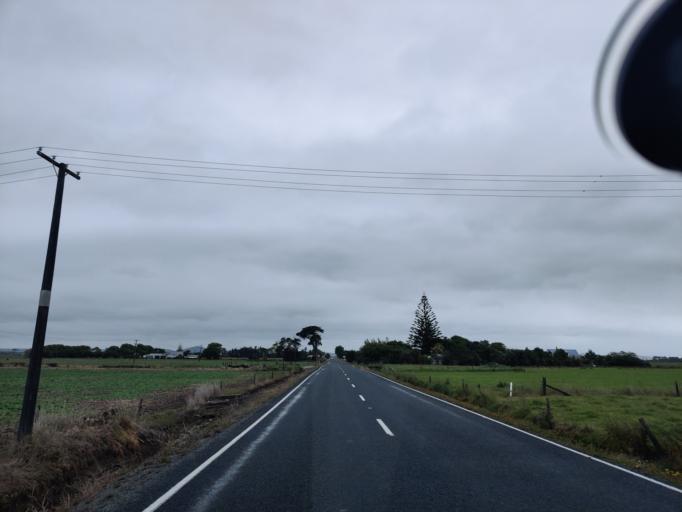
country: NZ
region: Northland
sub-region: Kaipara District
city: Dargaville
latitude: -36.1218
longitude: 173.9994
